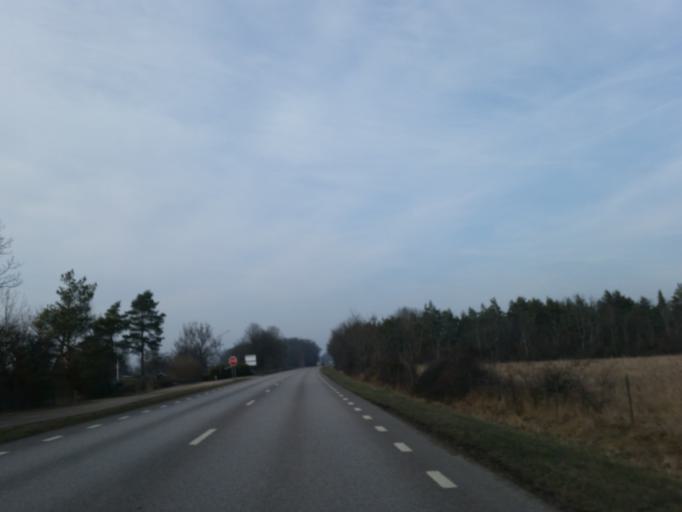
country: SE
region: Kalmar
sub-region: Borgholms Kommun
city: Borgholm
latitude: 56.8966
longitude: 16.7325
